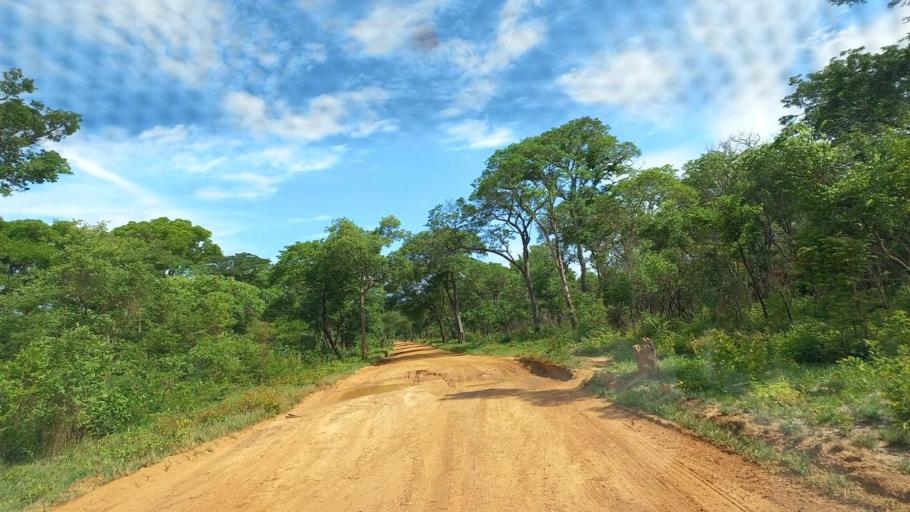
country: ZM
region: North-Western
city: Kabompo
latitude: -13.0846
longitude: 24.2204
